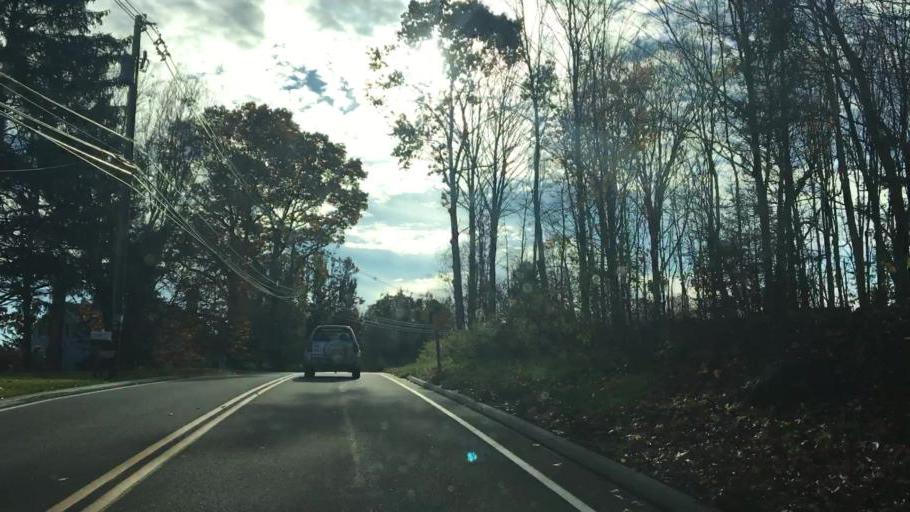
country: US
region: Connecticut
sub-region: New Haven County
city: Ansonia
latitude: 41.3720
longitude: -73.1226
